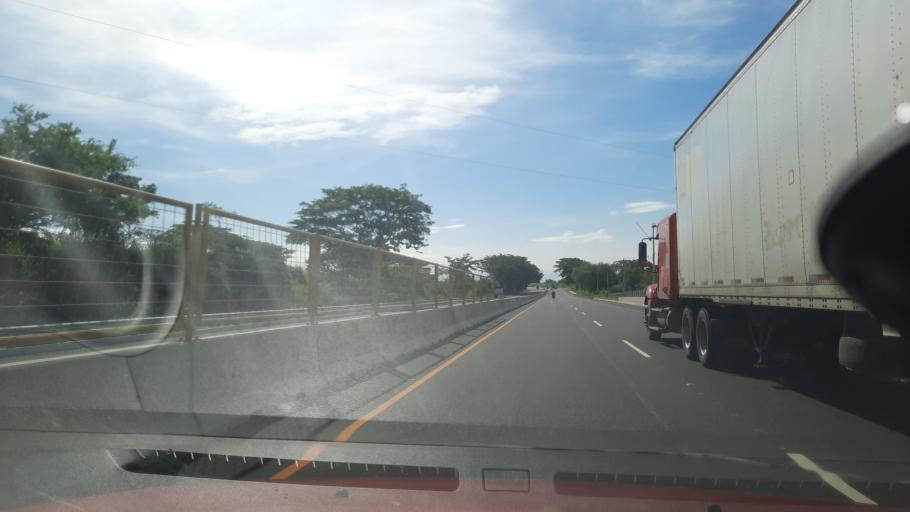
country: SV
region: La Paz
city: El Rosario
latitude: 13.4858
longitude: -88.9895
